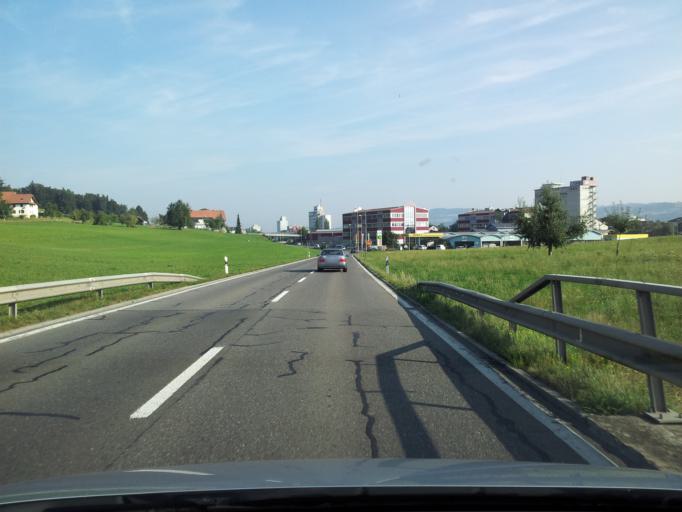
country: CH
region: Lucerne
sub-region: Sursee District
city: Sursee
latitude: 47.1609
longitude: 8.1043
